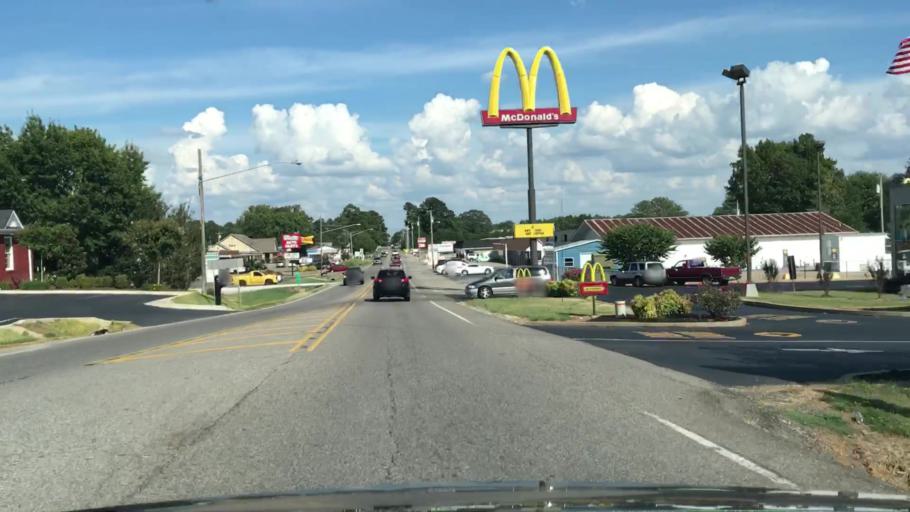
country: US
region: Tennessee
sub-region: Giles County
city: Ardmore
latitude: 34.9939
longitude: -86.8412
